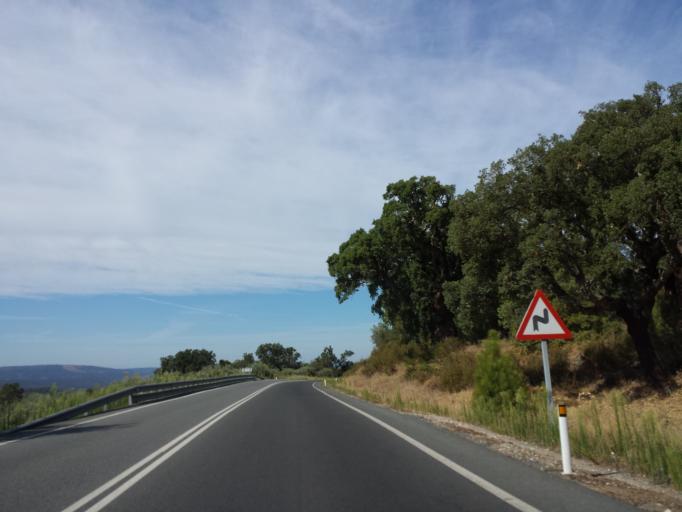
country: ES
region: Castille and Leon
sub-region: Provincia de Avila
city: Piedralaves
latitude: 40.3097
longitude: -4.7098
